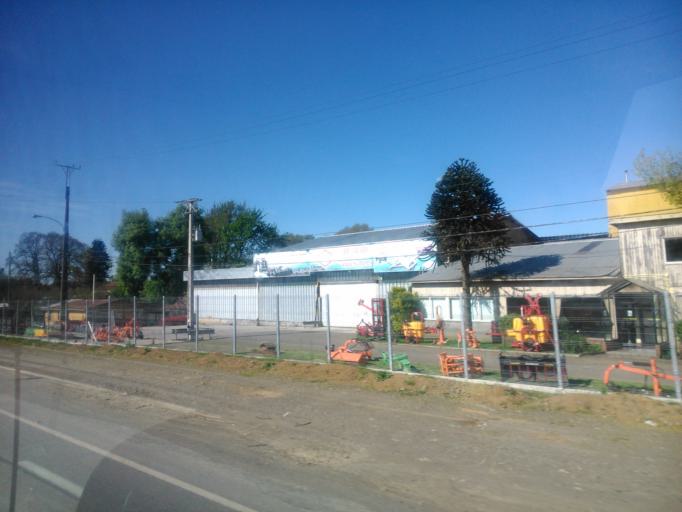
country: CL
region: Araucania
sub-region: Provincia de Cautin
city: Freire
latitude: -38.8694
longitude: -72.6172
